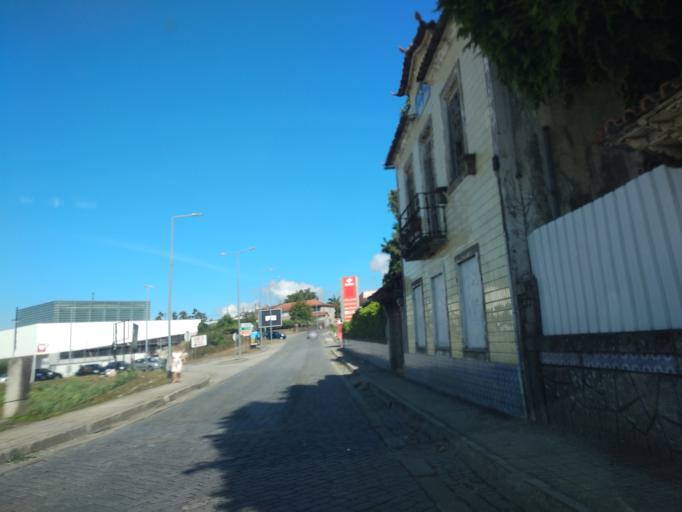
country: PT
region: Porto
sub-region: Pacos de Ferreira
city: Freamunde
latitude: 41.2874
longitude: -8.3361
